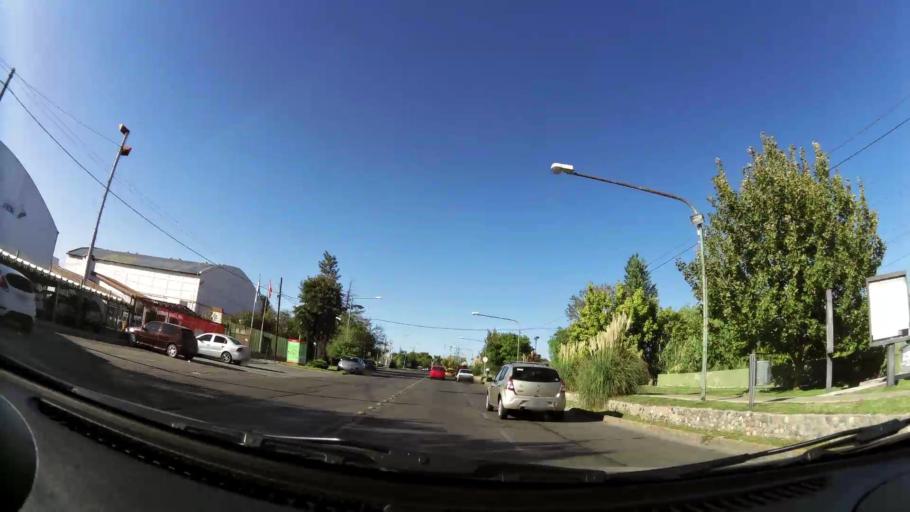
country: AR
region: Mendoza
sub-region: Departamento de Godoy Cruz
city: Godoy Cruz
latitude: -32.9363
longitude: -68.8406
